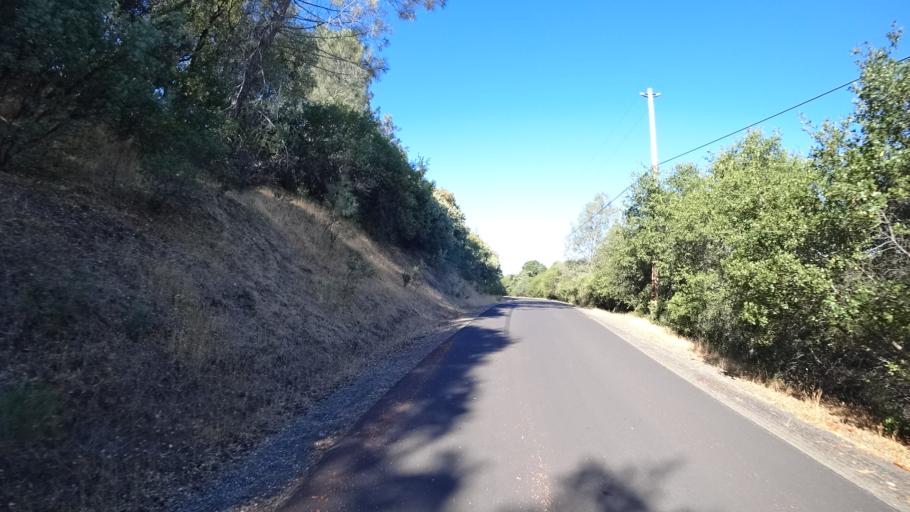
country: US
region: California
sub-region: Calaveras County
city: San Andreas
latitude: 38.2490
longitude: -120.7026
